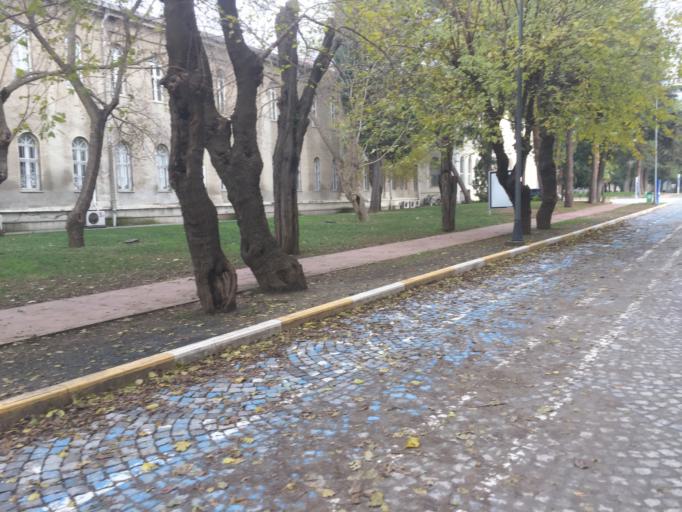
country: TR
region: Istanbul
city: merter keresteciler
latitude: 41.0248
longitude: 28.8899
